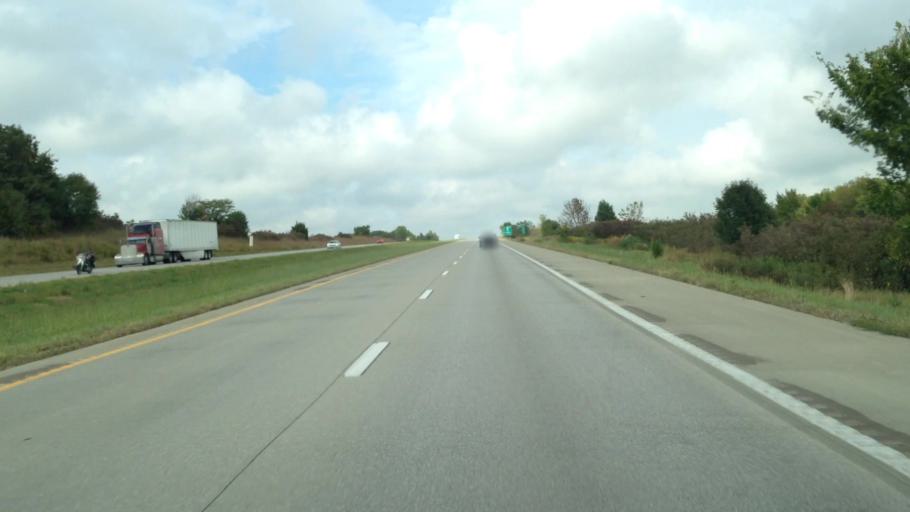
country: US
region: Missouri
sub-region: Clay County
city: Kearney
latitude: 39.4419
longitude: -94.3315
